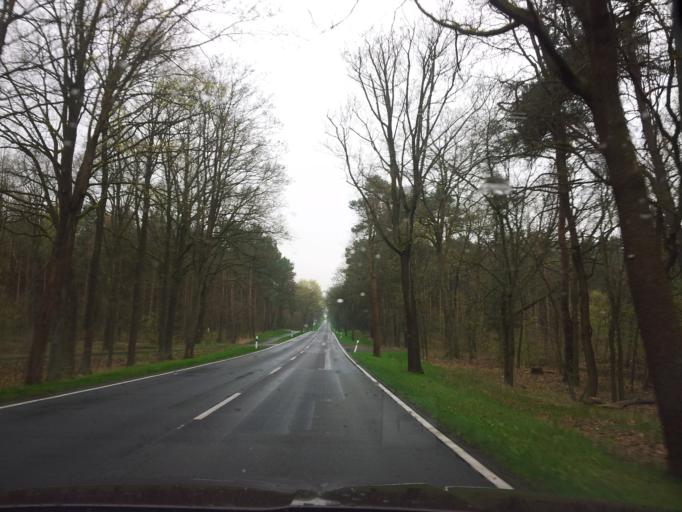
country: DE
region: Brandenburg
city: Treuenbrietzen
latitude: 52.0498
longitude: 12.8165
